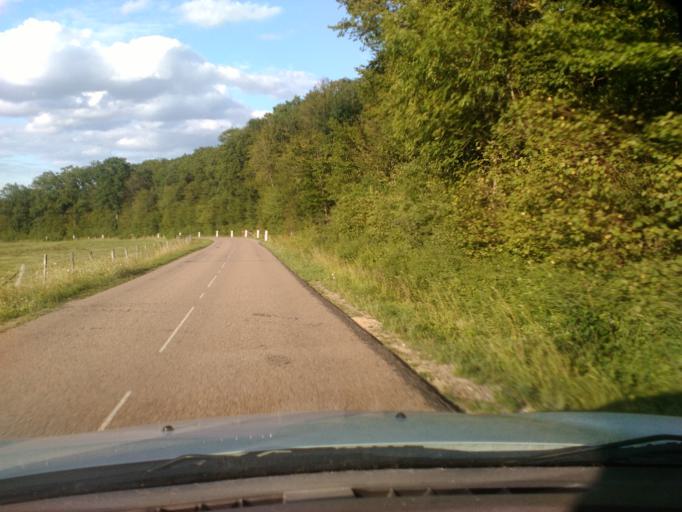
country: FR
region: Lorraine
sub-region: Departement des Vosges
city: Mirecourt
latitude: 48.3461
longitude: 6.0364
